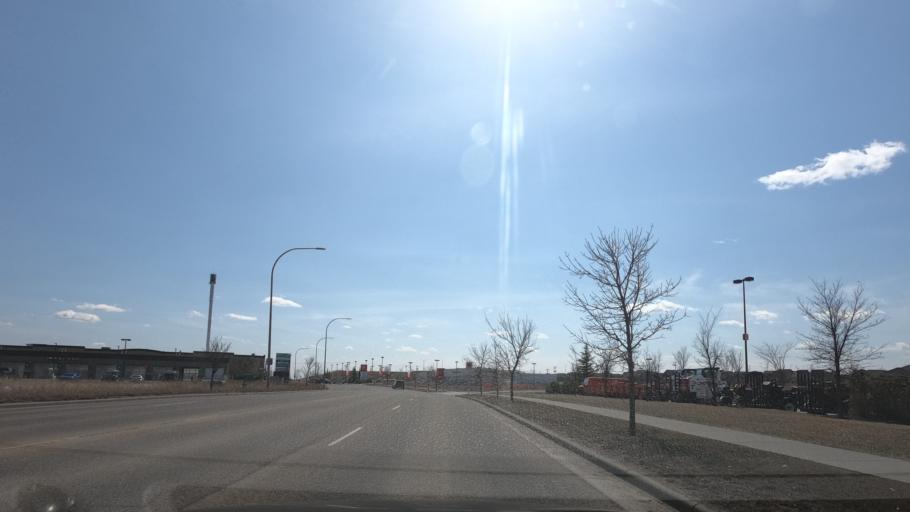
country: CA
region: Alberta
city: Airdrie
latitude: 51.2600
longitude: -114.0044
